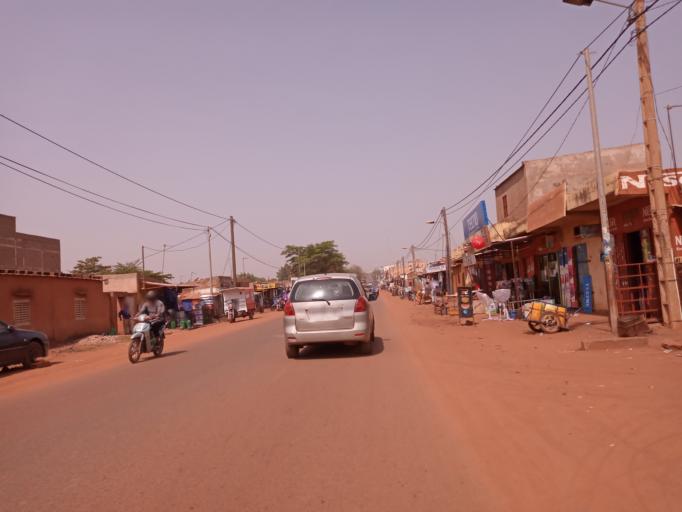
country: ML
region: Bamako
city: Bamako
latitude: 12.5888
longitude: -7.9845
